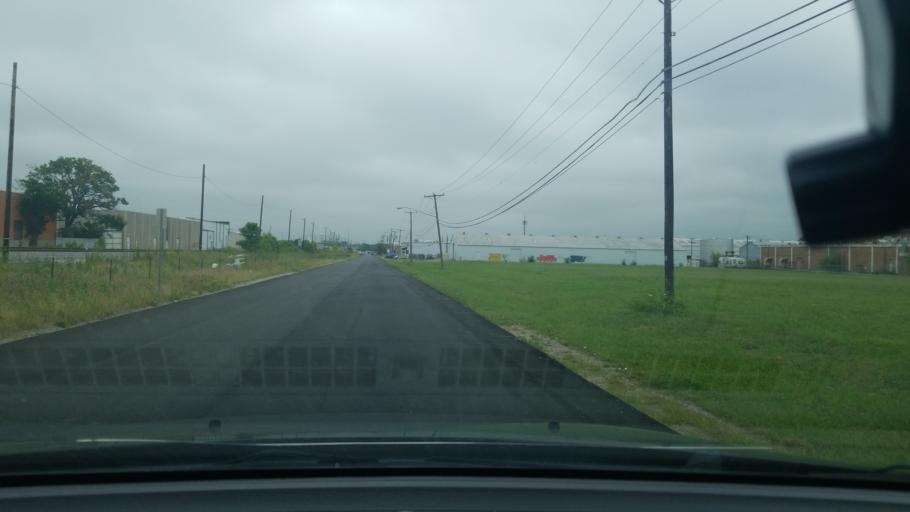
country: US
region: Texas
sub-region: Dallas County
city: Balch Springs
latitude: 32.7761
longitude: -96.6820
